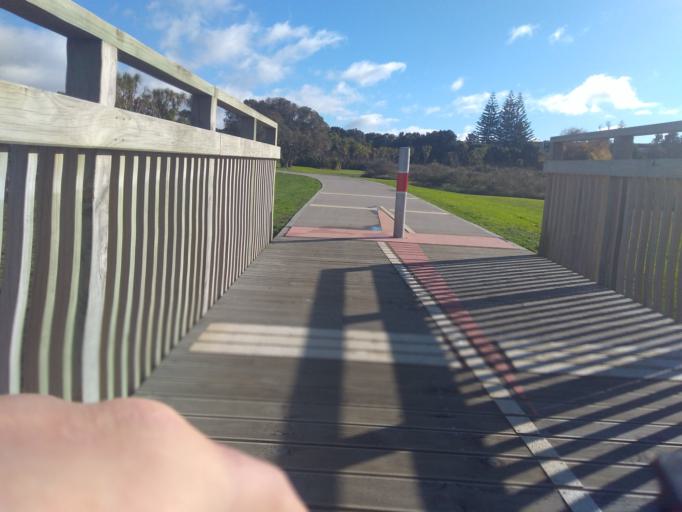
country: NZ
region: Auckland
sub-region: Auckland
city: Rosebank
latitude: -36.8702
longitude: 174.6986
